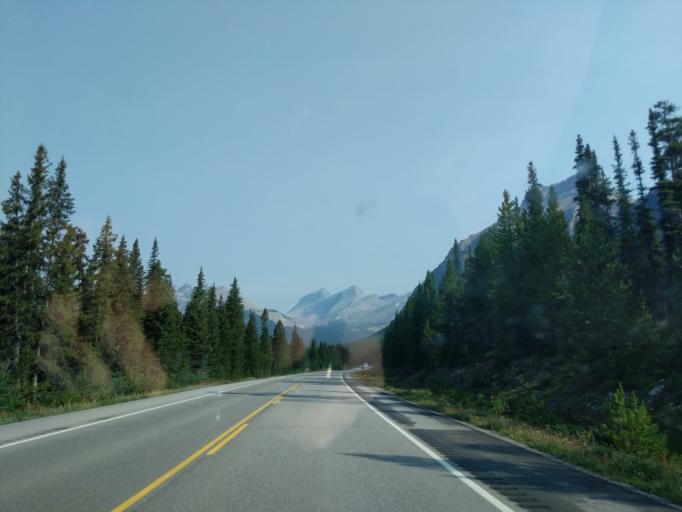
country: CA
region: Alberta
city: Lake Louise
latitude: 51.6127
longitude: -116.3146
